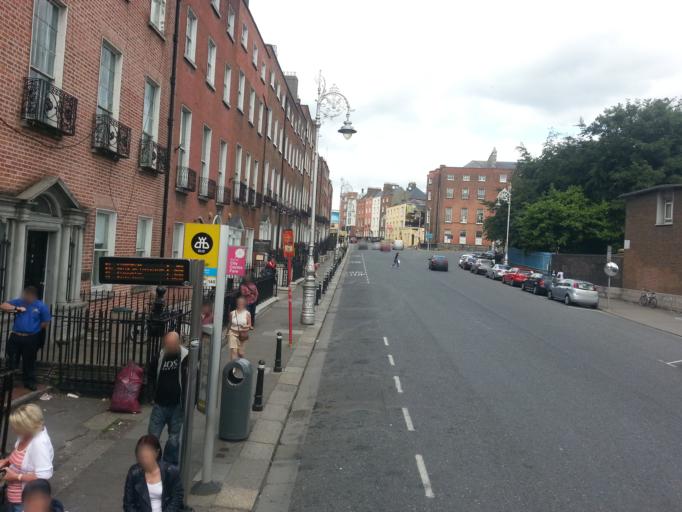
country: IE
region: Leinster
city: Drumcondra
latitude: 53.3527
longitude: -6.2640
